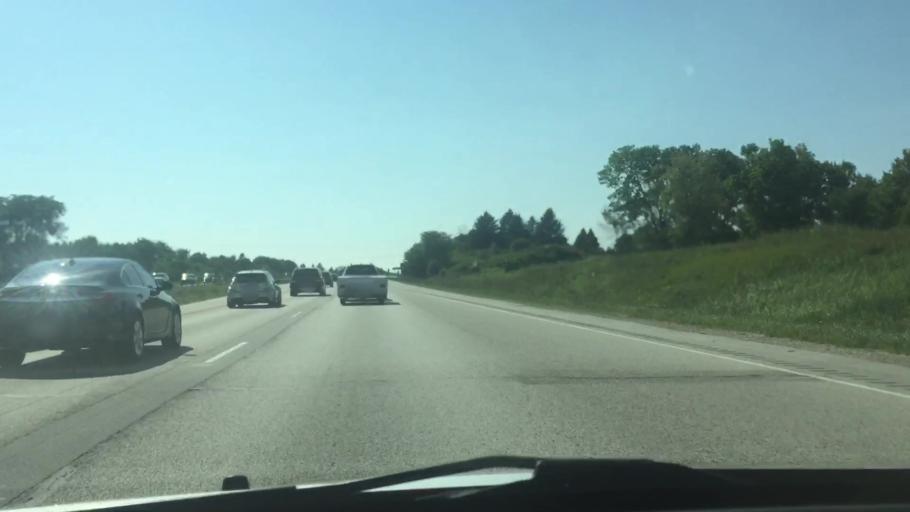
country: US
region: Wisconsin
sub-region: Waukesha County
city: Delafield
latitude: 43.0543
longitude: -88.4111
